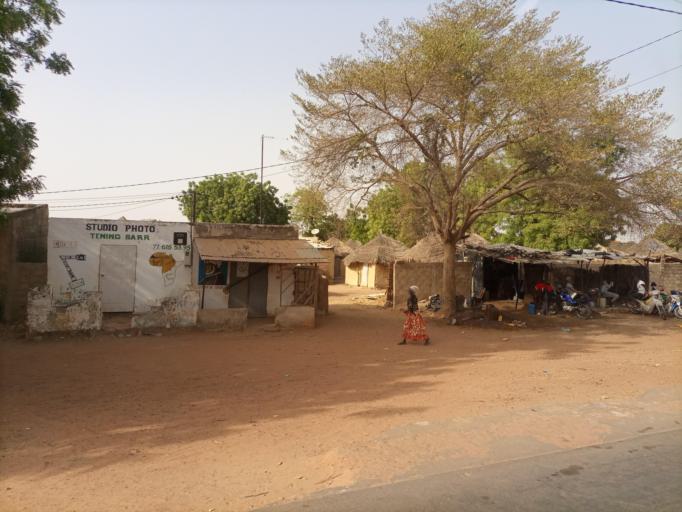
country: SN
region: Fatick
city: Foundiougne
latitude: 14.1214
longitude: -16.4356
